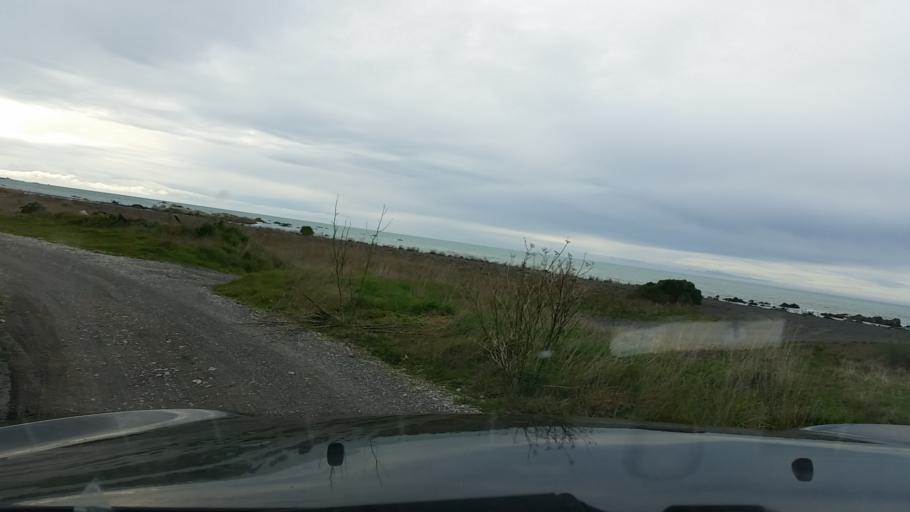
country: NZ
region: Marlborough
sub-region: Marlborough District
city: Blenheim
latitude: -41.9261
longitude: 174.0956
